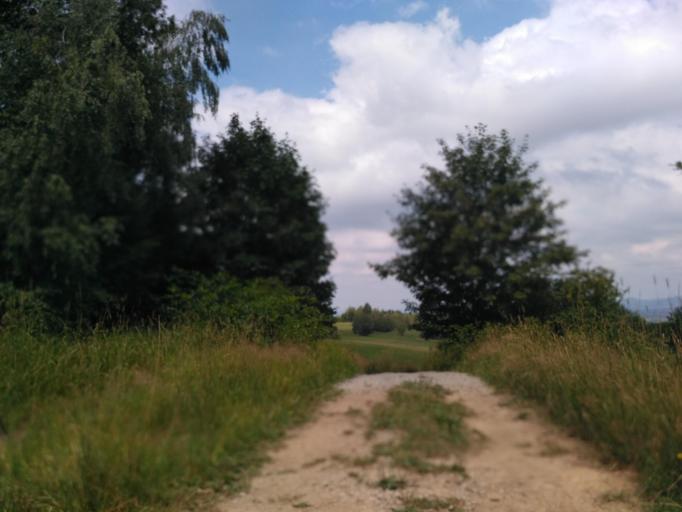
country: PL
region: Subcarpathian Voivodeship
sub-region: Powiat krosnienski
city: Iwonicz-Zdroj
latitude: 49.5724
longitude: 21.8105
